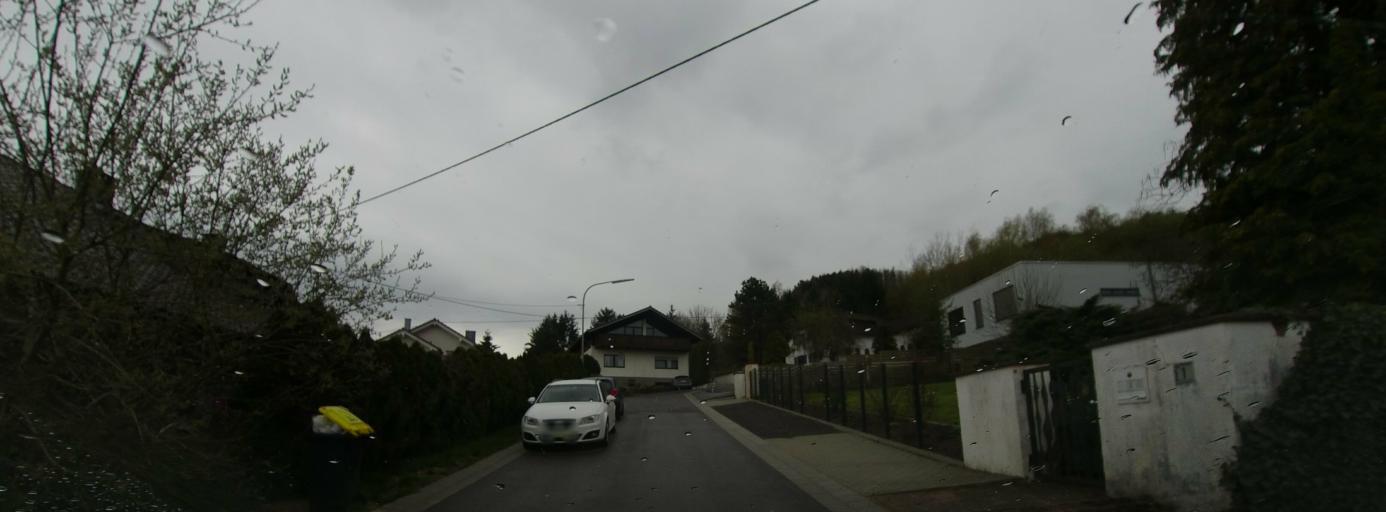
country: DE
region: Saarland
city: Losheim
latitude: 49.5026
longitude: 6.7422
